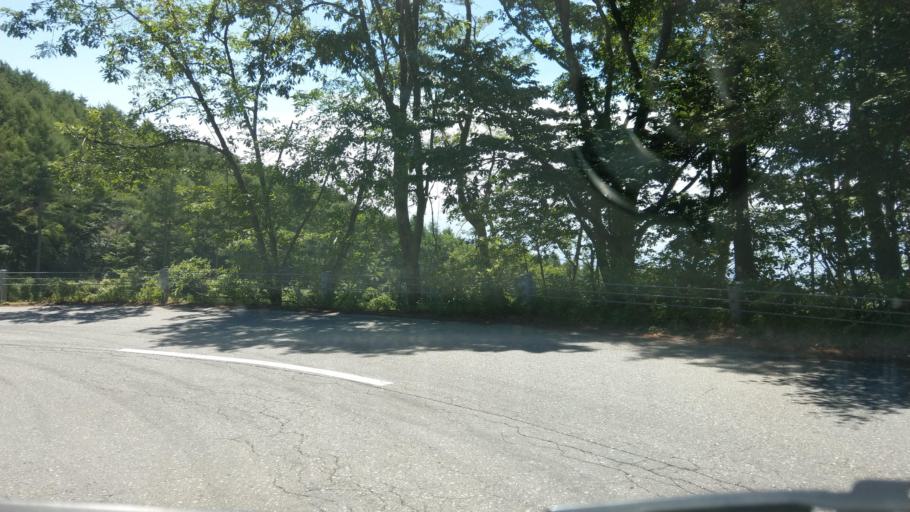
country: JP
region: Nagano
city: Komoro
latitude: 36.3876
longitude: 138.4654
